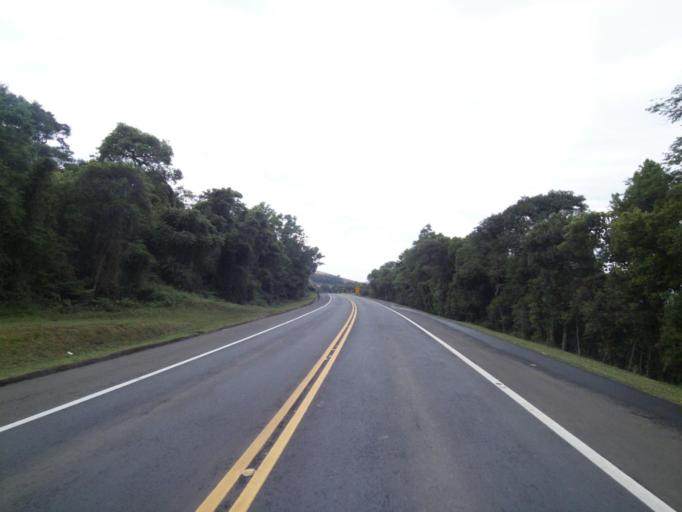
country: BR
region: Parana
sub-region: Irati
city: Irati
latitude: -25.4519
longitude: -50.6439
